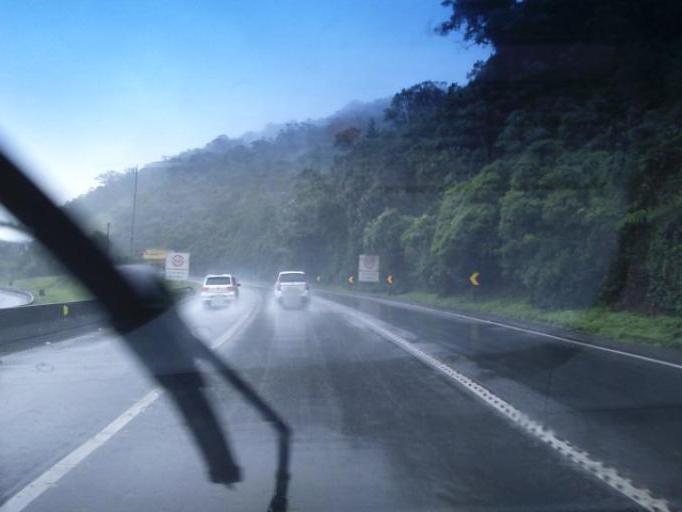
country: BR
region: Parana
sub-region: Guaratuba
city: Guaratuba
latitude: -25.8647
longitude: -48.9340
